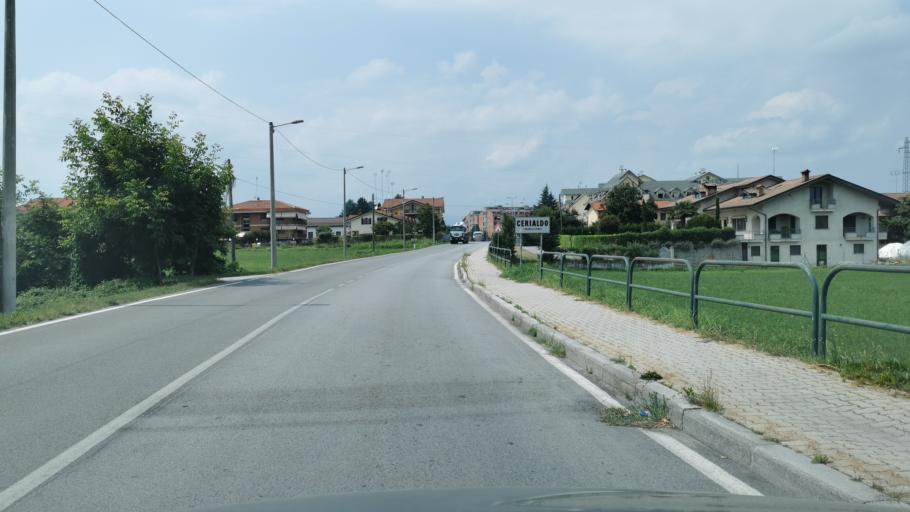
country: IT
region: Piedmont
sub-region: Provincia di Cuneo
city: Cuneo
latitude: 44.3981
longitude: 7.5346
